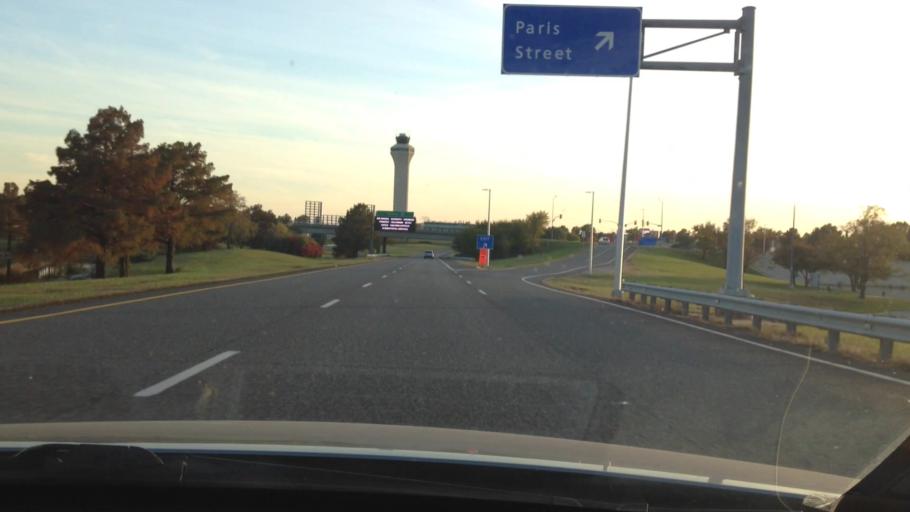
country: US
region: Missouri
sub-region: Platte County
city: Weatherby Lake
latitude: 39.3046
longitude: -94.7129
